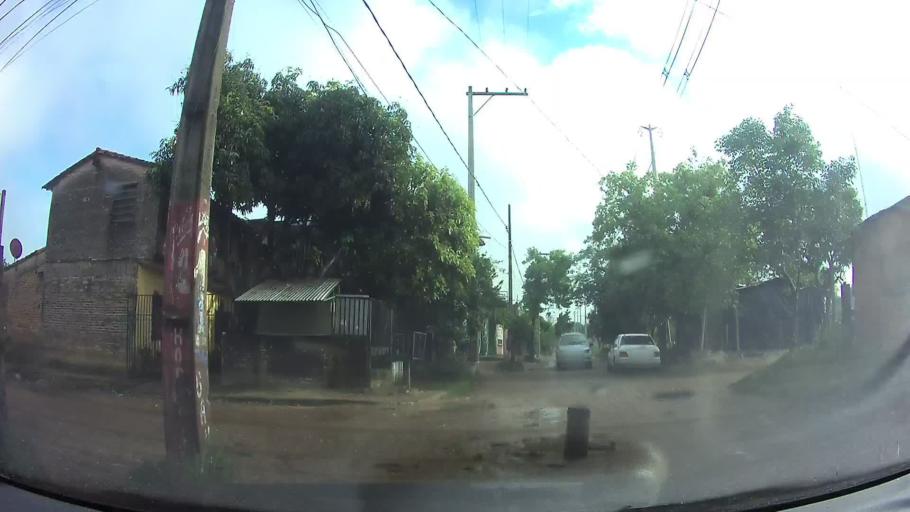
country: PY
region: Asuncion
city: Asuncion
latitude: -25.2474
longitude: -57.5828
